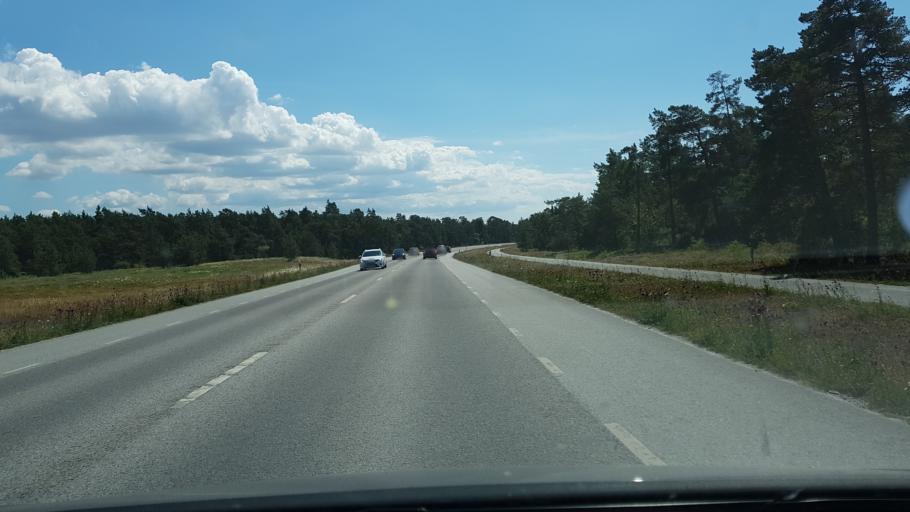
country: SE
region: Gotland
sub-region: Gotland
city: Vibble
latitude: 57.5522
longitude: 18.2029
